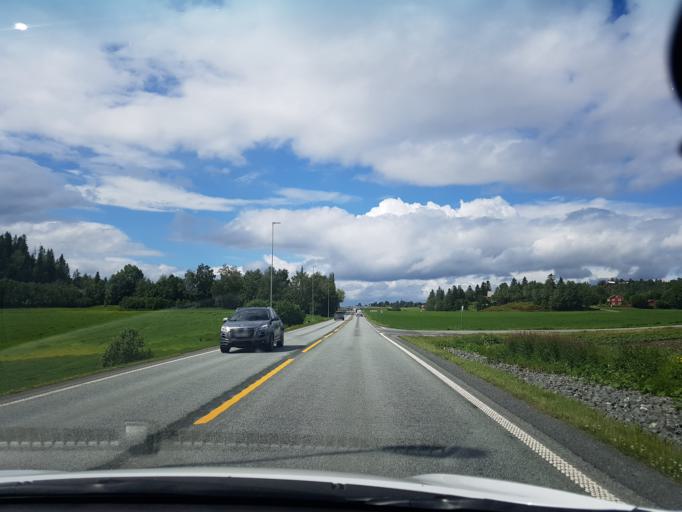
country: NO
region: Nord-Trondelag
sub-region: Stjordal
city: Stjordal
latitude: 63.5195
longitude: 10.8557
